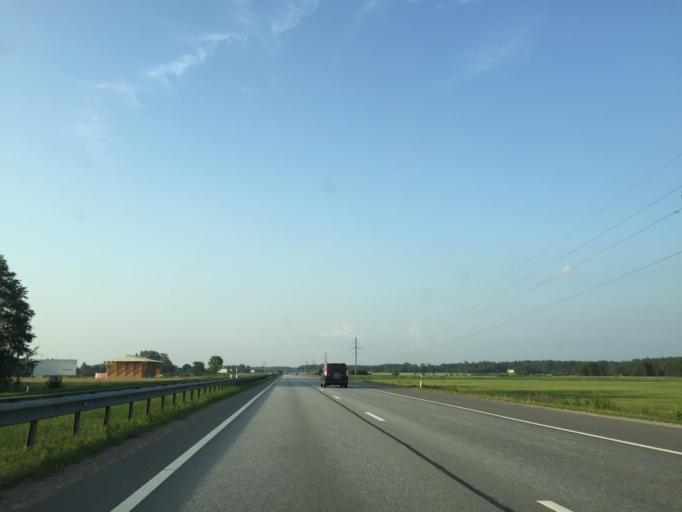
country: LV
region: Marupe
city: Marupe
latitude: 56.8233
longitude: 24.0233
